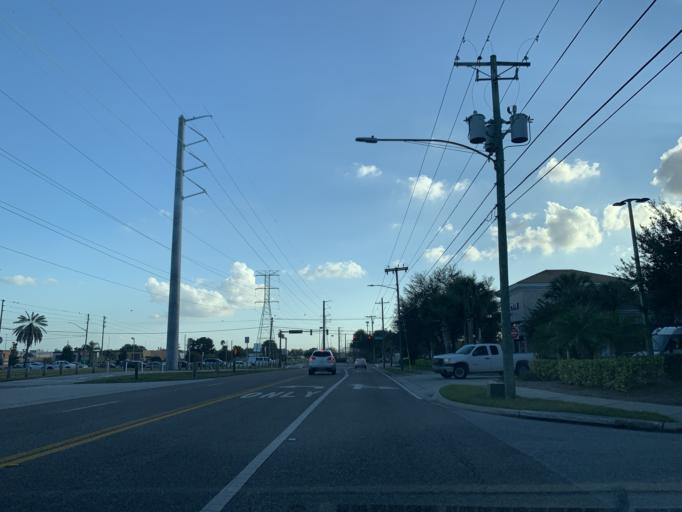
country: US
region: Florida
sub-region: Pinellas County
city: South Highpoint
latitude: 27.9616
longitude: -82.7341
